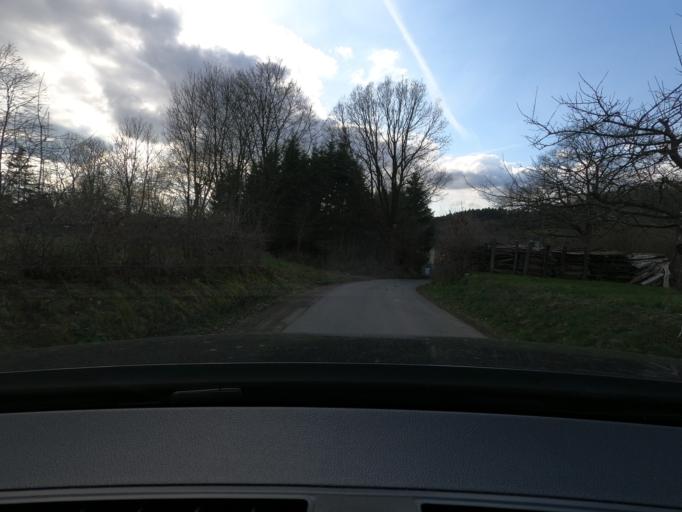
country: DE
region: North Rhine-Westphalia
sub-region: Regierungsbezirk Arnsberg
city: Herscheid
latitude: 51.1262
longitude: 7.7788
